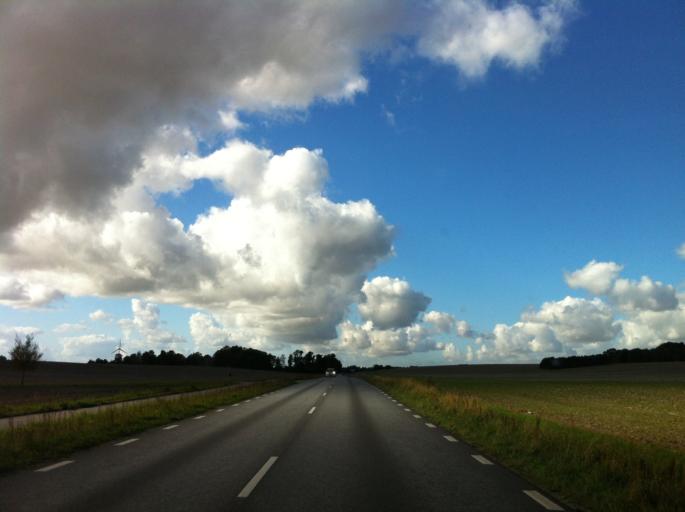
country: SE
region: Skane
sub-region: Eslovs Kommun
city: Eslov
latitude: 55.7565
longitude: 13.3408
